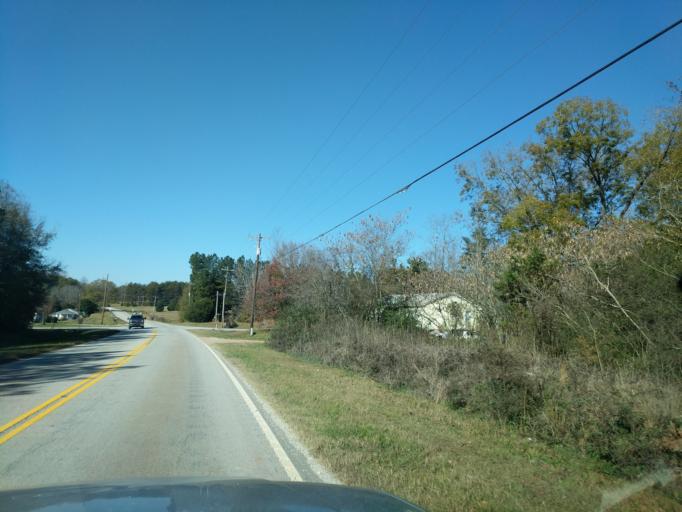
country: US
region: South Carolina
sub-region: Greenville County
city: Tigerville
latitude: 35.0282
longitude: -82.4079
